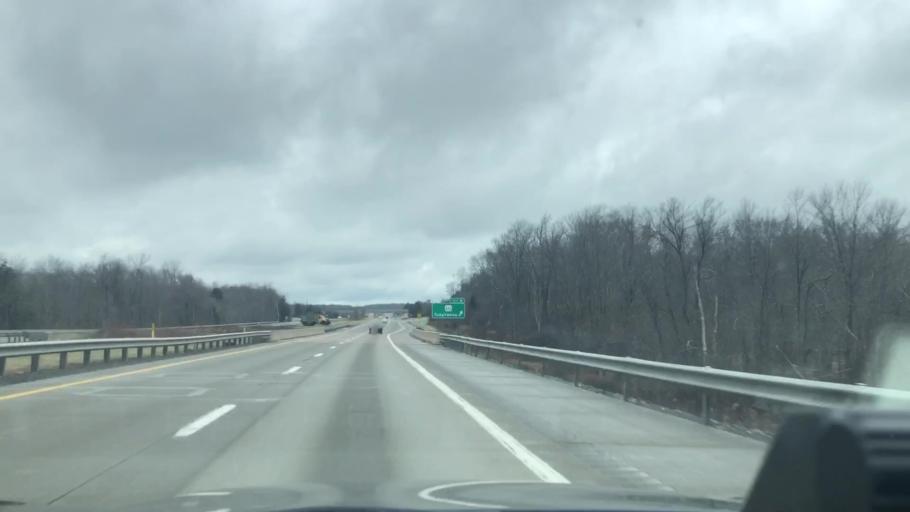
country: US
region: Pennsylvania
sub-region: Monroe County
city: Pocono Pines
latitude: 41.1675
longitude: -75.4240
